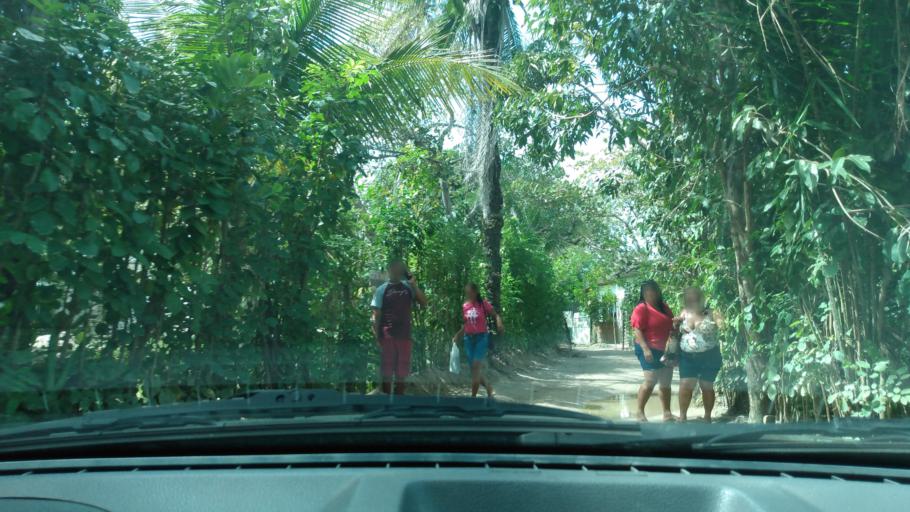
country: BR
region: Pernambuco
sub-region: Cabo De Santo Agostinho
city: Cabo
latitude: -8.3546
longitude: -34.9662
